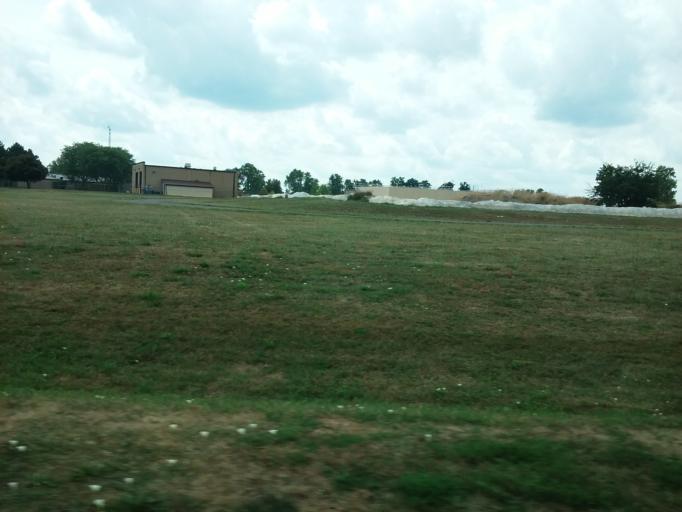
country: US
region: Ohio
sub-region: Hancock County
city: Findlay
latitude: 41.0502
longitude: -83.6685
